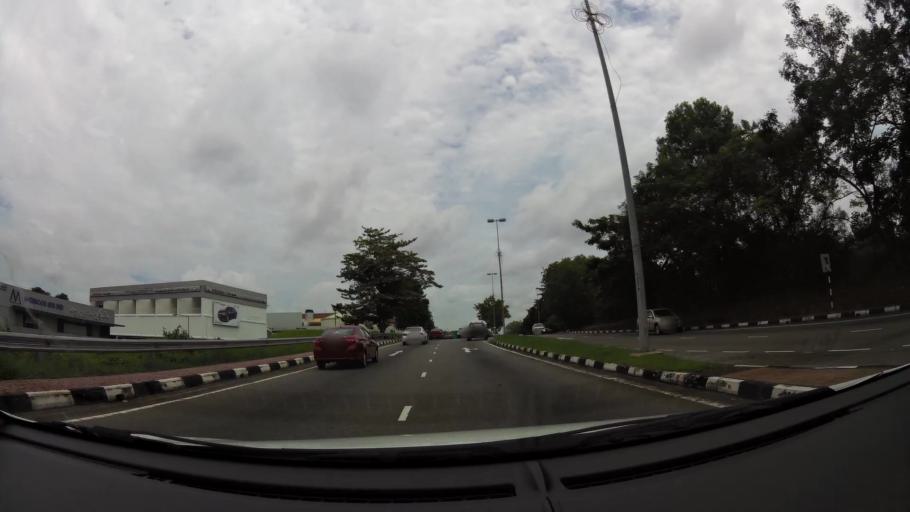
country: BN
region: Brunei and Muara
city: Bandar Seri Begawan
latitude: 4.9092
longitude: 114.9137
